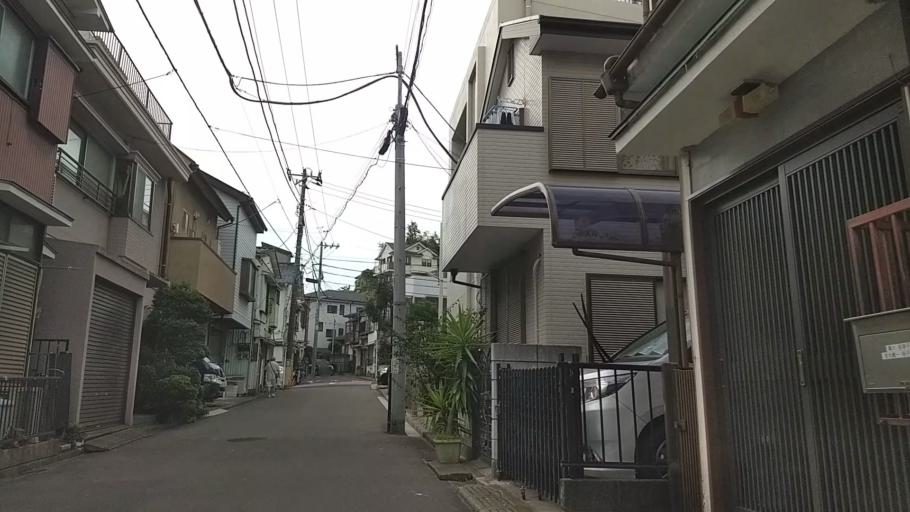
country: JP
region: Kanagawa
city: Yokohama
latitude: 35.4397
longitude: 139.6134
